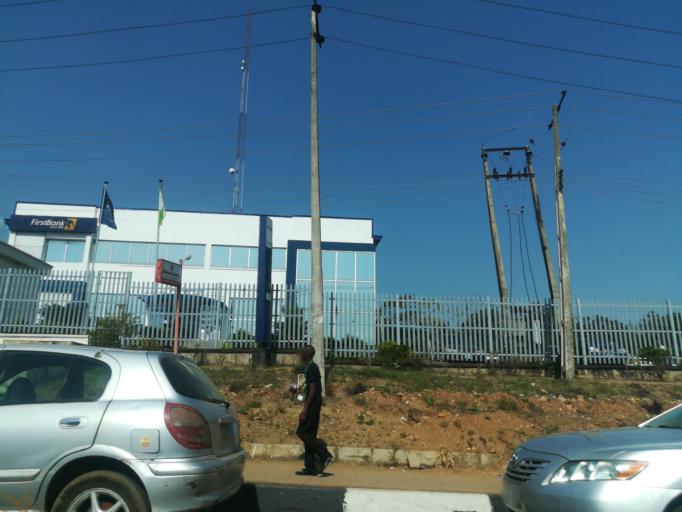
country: NG
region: Ogun
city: Abeokuta
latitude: 7.1325
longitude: 3.3326
